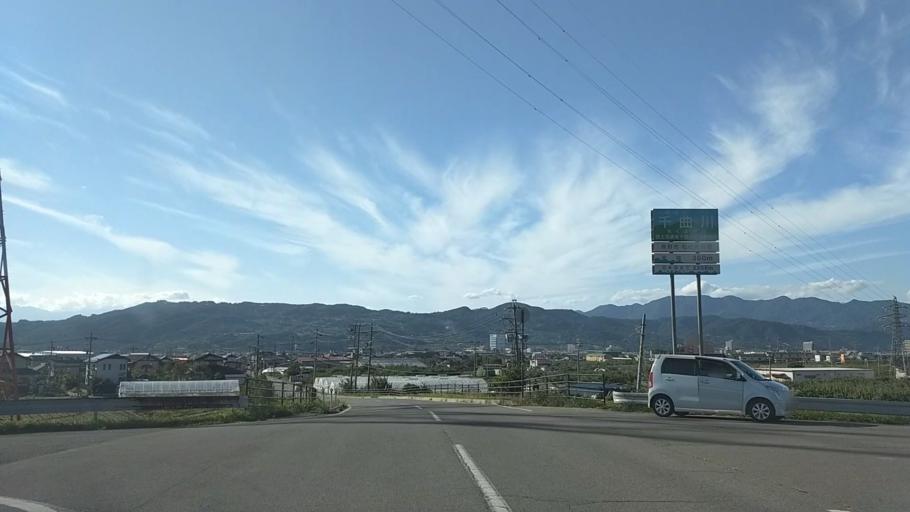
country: JP
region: Nagano
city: Nagano-shi
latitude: 36.5636
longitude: 138.1545
